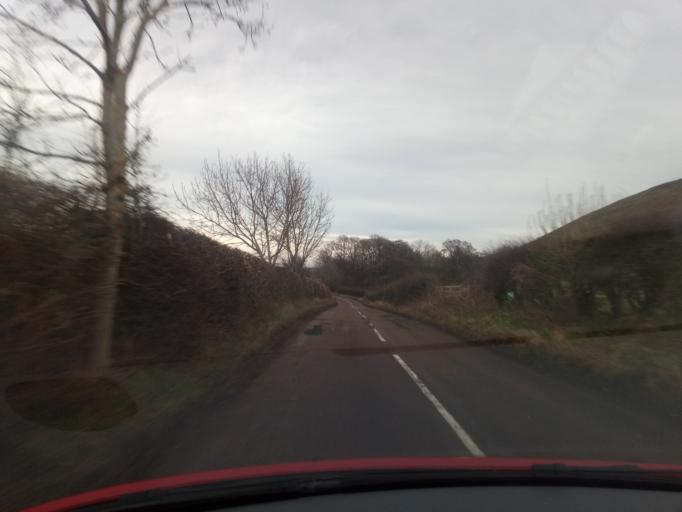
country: GB
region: England
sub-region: Northumberland
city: Kirknewton
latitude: 55.5643
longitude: -2.0932
